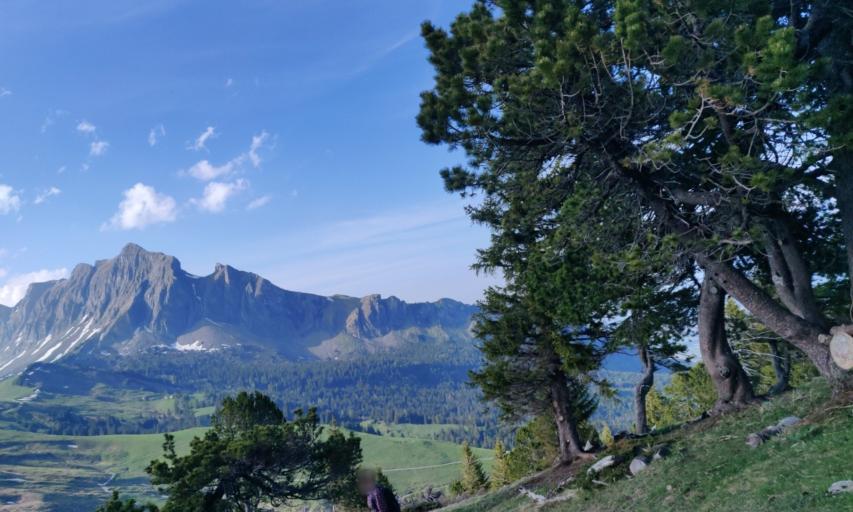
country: CH
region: Saint Gallen
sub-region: Wahlkreis Sarganserland
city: Sargans
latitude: 47.0709
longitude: 9.4331
